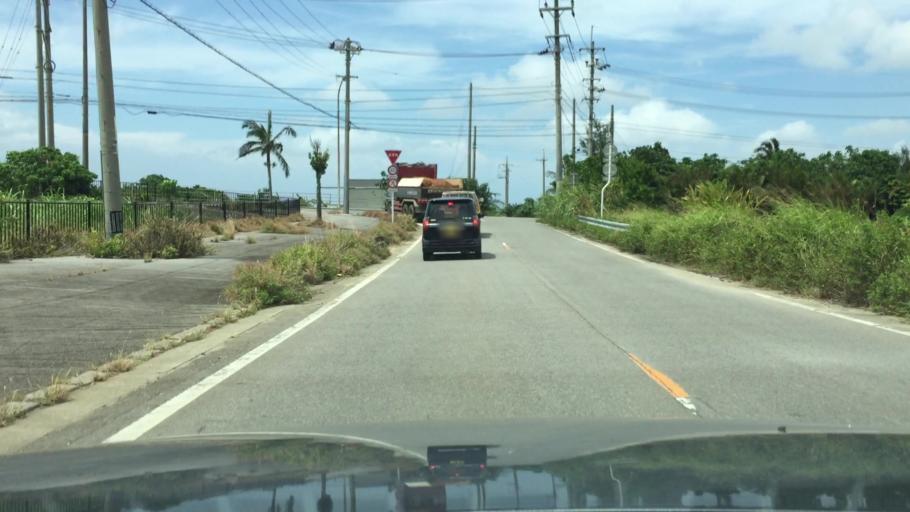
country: JP
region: Okinawa
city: Ishigaki
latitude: 24.4533
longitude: 124.2059
